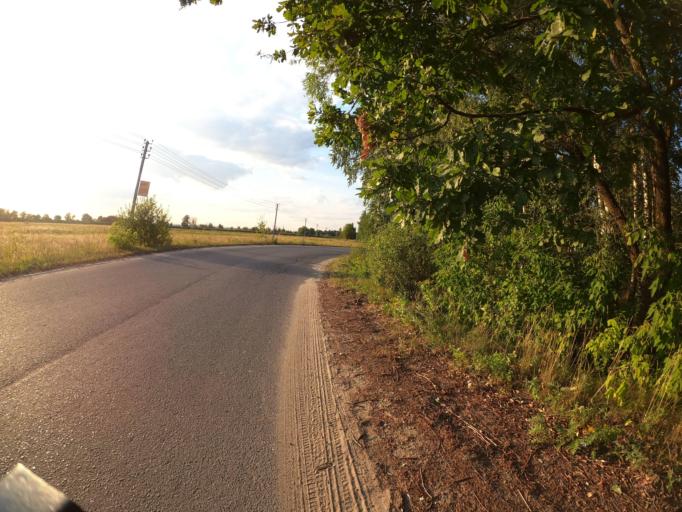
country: RU
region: Moskovskaya
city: Malyshevo
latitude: 55.5152
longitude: 38.2839
